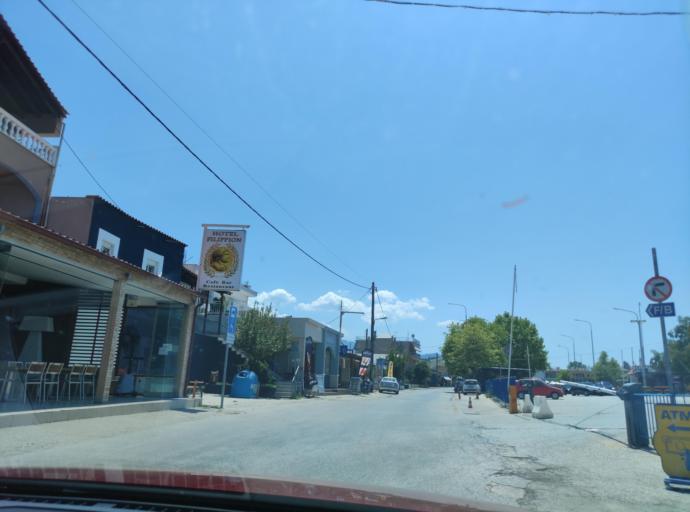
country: GR
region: East Macedonia and Thrace
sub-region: Nomos Kavalas
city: Keramoti
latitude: 40.8574
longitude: 24.7031
